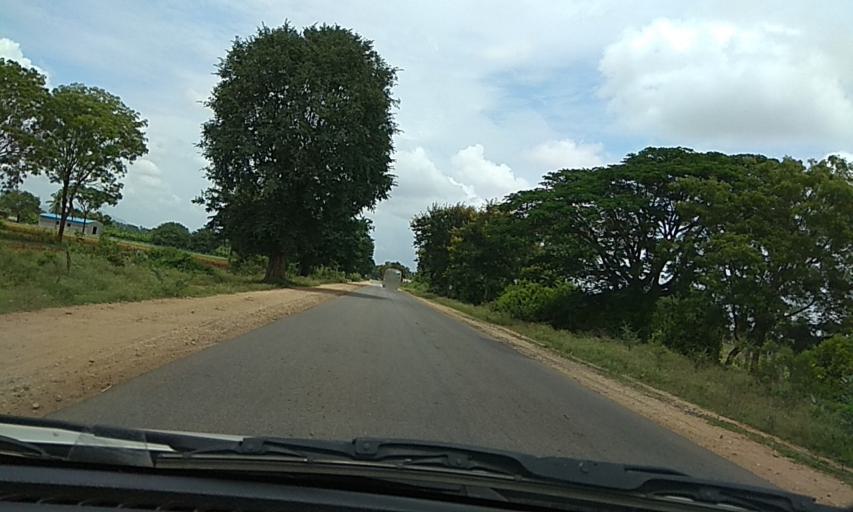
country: IN
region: Karnataka
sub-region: Chamrajnagar
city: Gundlupet
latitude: 11.8110
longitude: 76.7332
